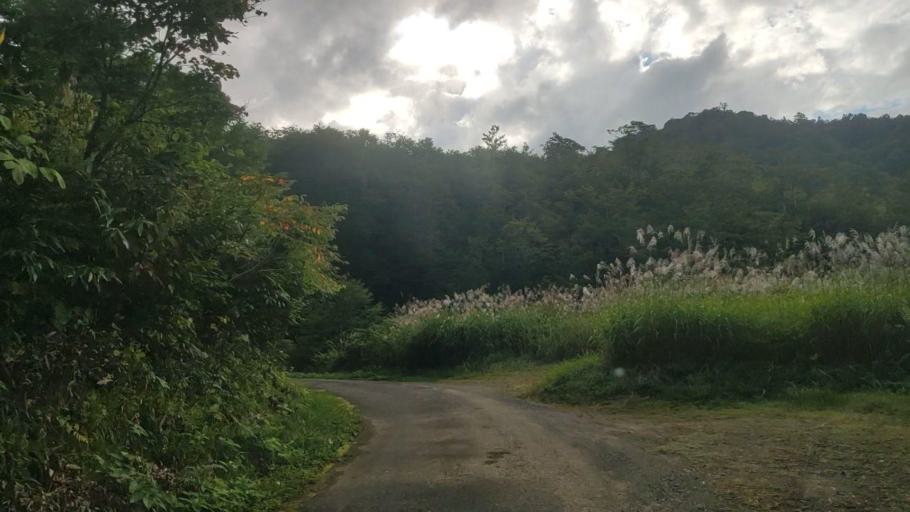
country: JP
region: Toyama
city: Yatsuomachi-higashikumisaka
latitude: 36.3473
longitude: 137.0665
